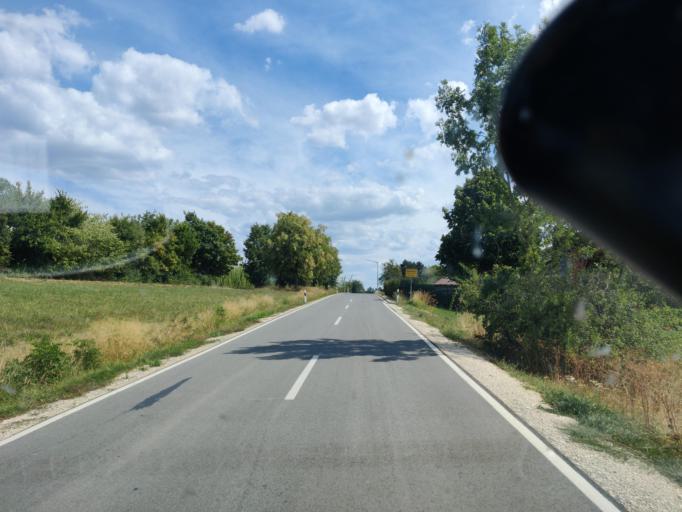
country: DE
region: Bavaria
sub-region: Regierungsbezirk Mittelfranken
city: Heideck
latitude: 49.1223
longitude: 11.1297
